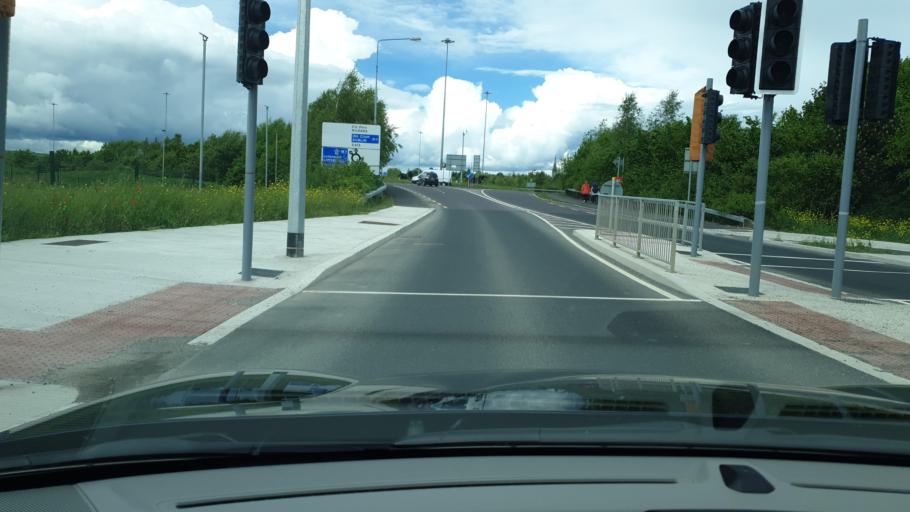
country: IE
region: Leinster
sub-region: Kildare
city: Kildare
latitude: 53.1499
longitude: -6.9191
